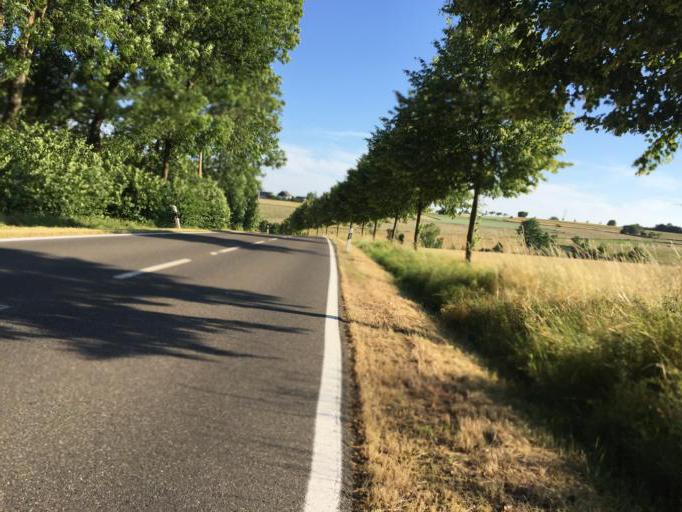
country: DE
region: Rheinland-Pfalz
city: Hartlingen
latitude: 50.5368
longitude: 7.9133
